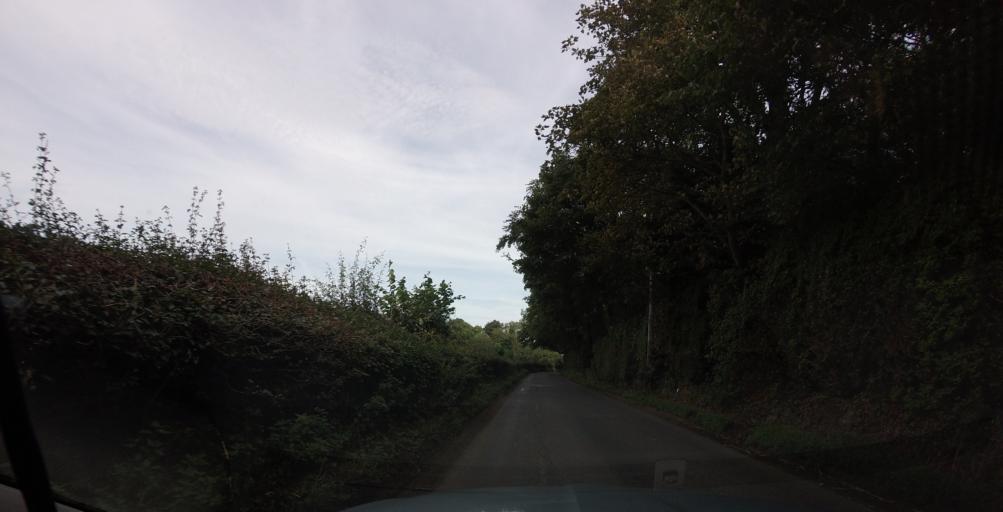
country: GB
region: England
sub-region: North Yorkshire
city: Ripon
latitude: 54.1129
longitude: -1.5181
